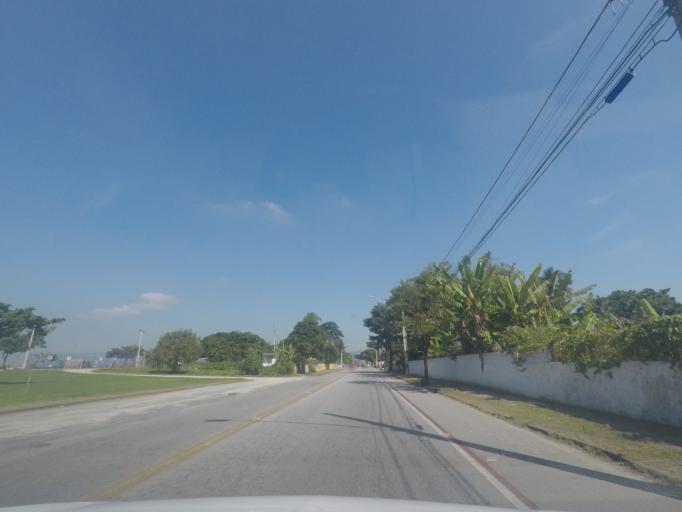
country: BR
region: Parana
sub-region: Paranagua
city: Paranagua
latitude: -25.5356
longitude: -48.5279
